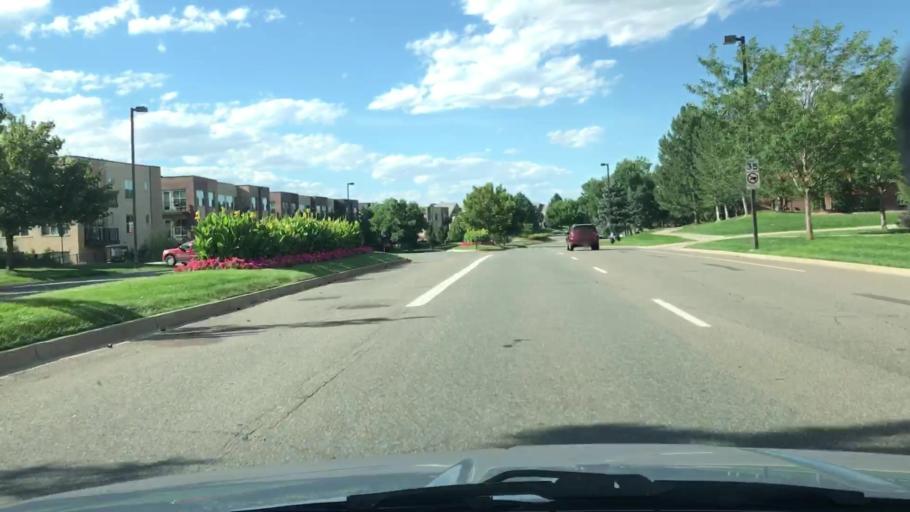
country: US
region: Colorado
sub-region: Arapahoe County
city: Greenwood Village
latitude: 39.6285
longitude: -104.9112
